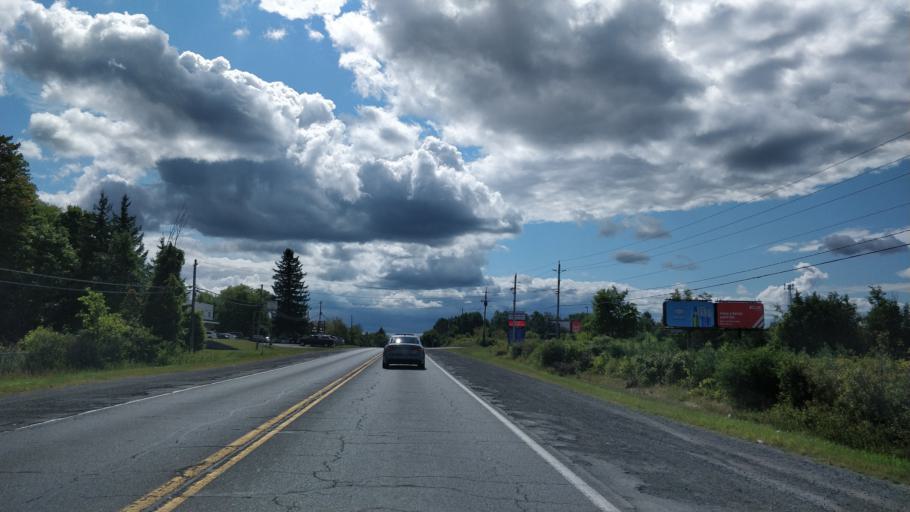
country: CA
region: Ontario
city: Ottawa
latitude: 45.2923
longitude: -75.5774
